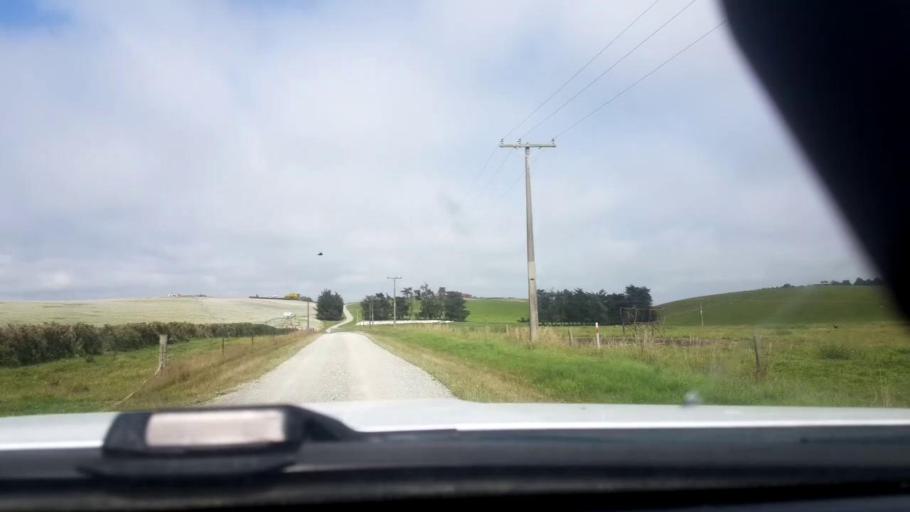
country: NZ
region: Canterbury
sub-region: Timaru District
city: Timaru
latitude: -44.3300
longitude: 171.2018
